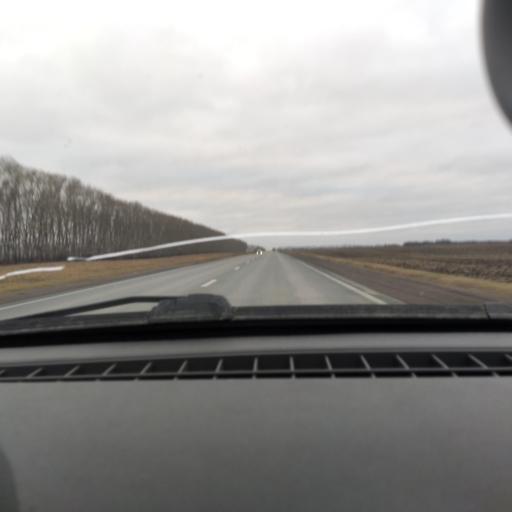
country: RU
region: Bashkortostan
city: Ulukulevo
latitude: 54.4086
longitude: 56.3110
